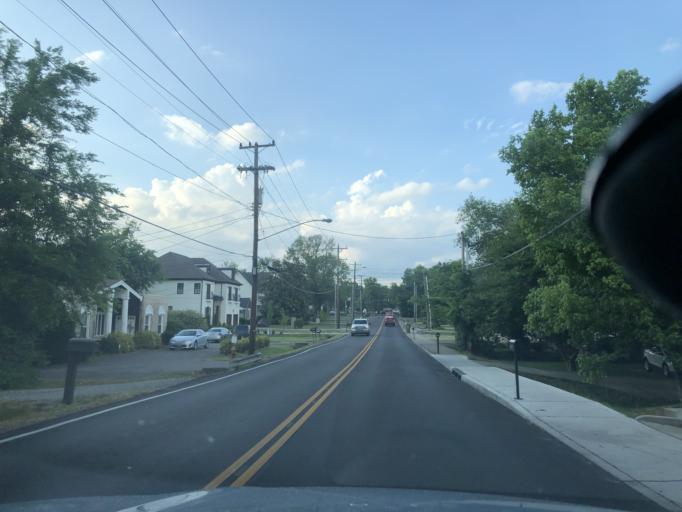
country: US
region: Tennessee
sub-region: Davidson County
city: Oak Hill
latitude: 36.1024
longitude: -86.8089
